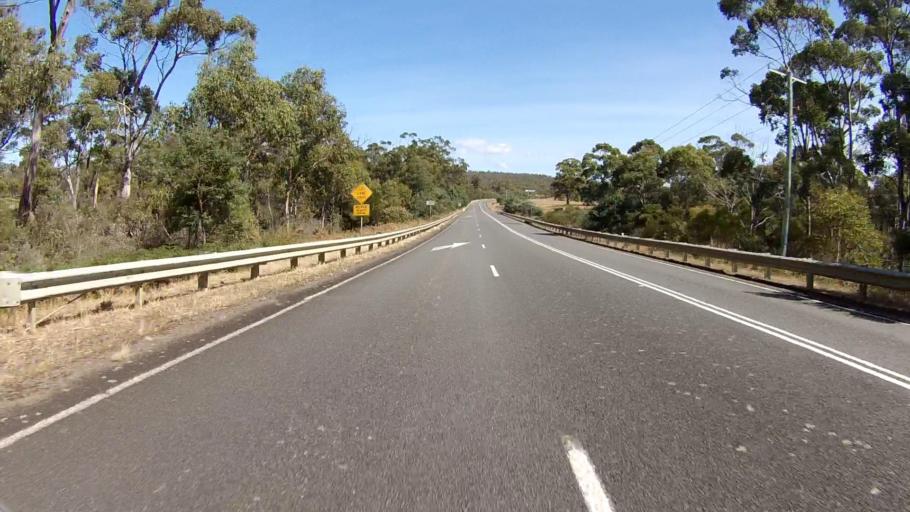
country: AU
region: Tasmania
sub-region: Sorell
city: Sorell
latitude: -42.5754
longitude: 147.8189
